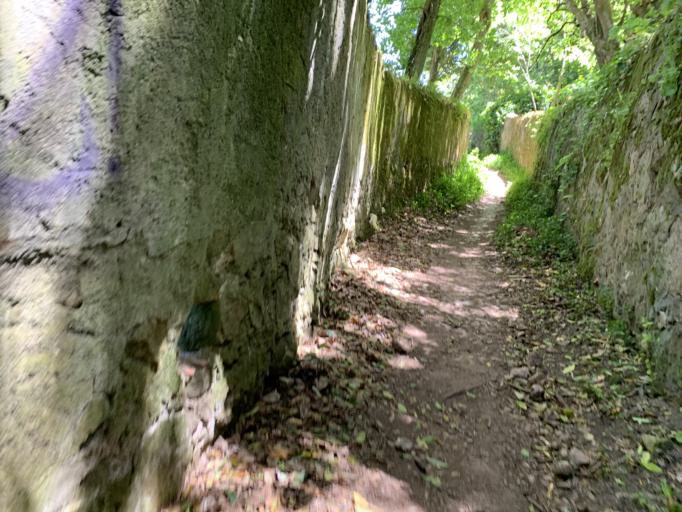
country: PT
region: Lisbon
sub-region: Sintra
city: Sintra
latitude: 38.7944
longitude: -9.3980
